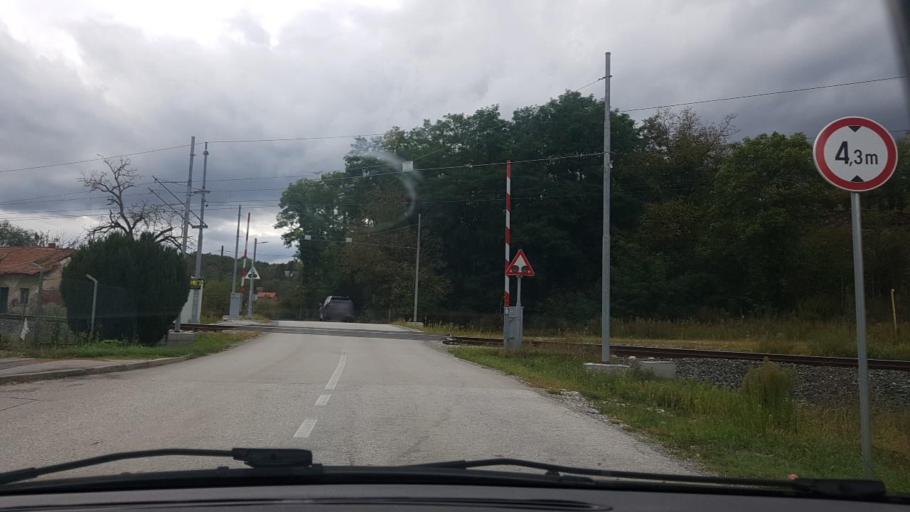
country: HR
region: Zagrebacka
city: Jakovlje
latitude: 45.9577
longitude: 15.8257
